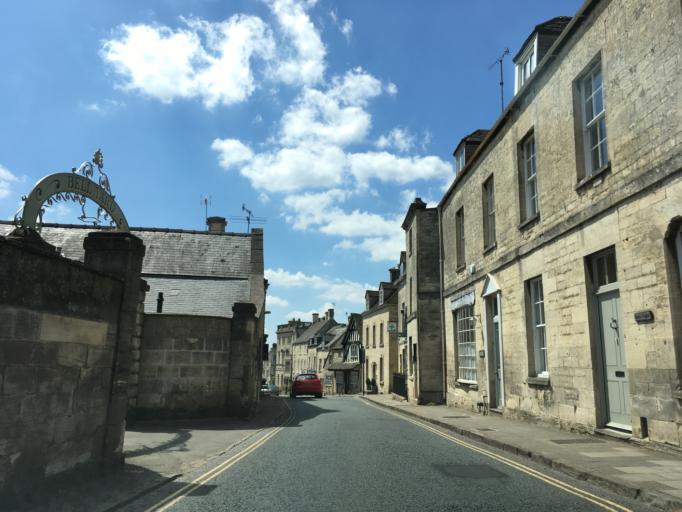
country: GB
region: England
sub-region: Gloucestershire
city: Painswick
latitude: 51.7867
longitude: -2.1939
